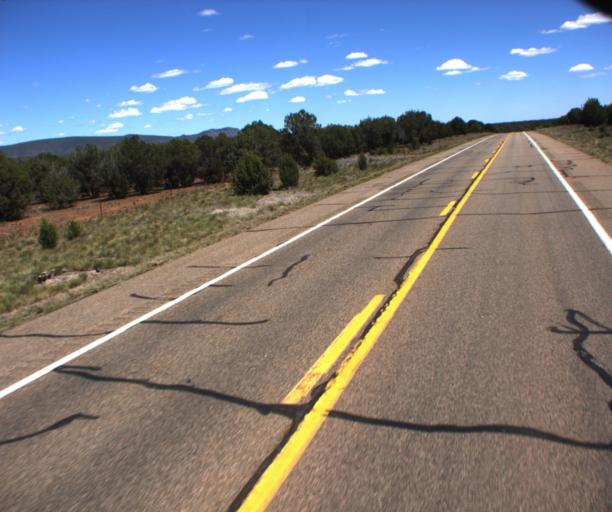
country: US
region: Arizona
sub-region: Yavapai County
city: Paulden
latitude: 35.0901
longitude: -112.4139
